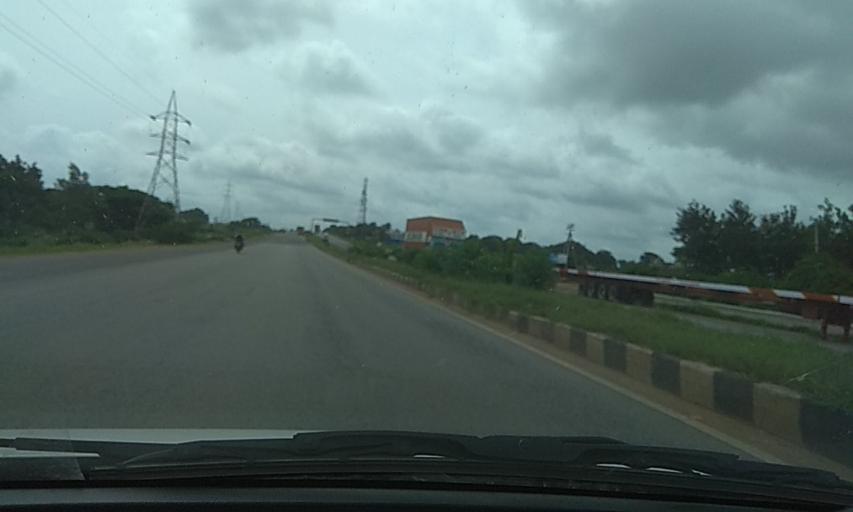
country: IN
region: Karnataka
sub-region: Davanagere
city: Mayakonda
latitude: 14.4150
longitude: 75.9850
